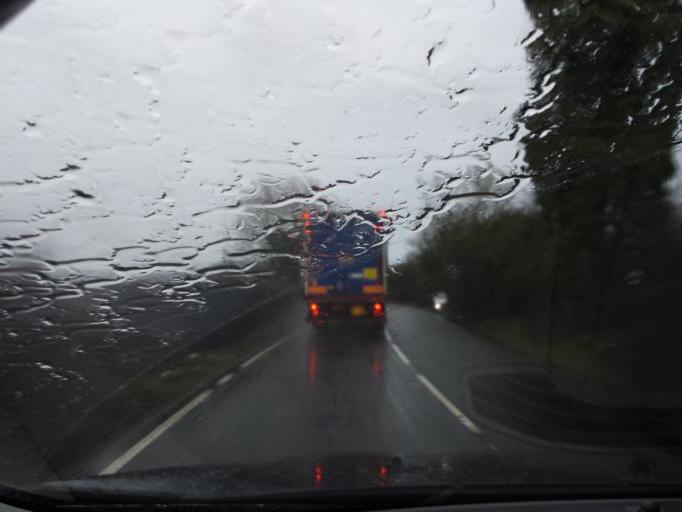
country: GB
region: Northern Ireland
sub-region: Antrim Borough
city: Antrim
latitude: 54.6666
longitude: -6.2199
